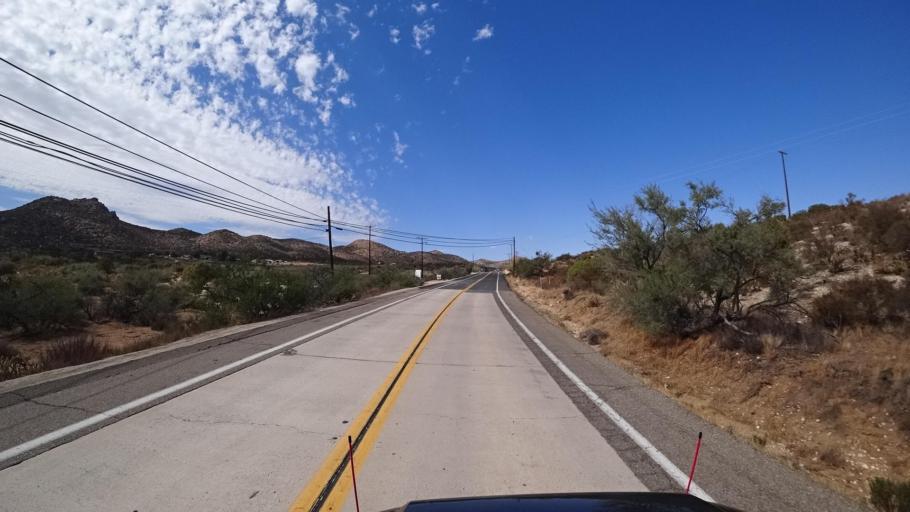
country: MX
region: Baja California
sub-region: Tecate
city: Cereso del Hongo
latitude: 32.6246
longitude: -116.2212
